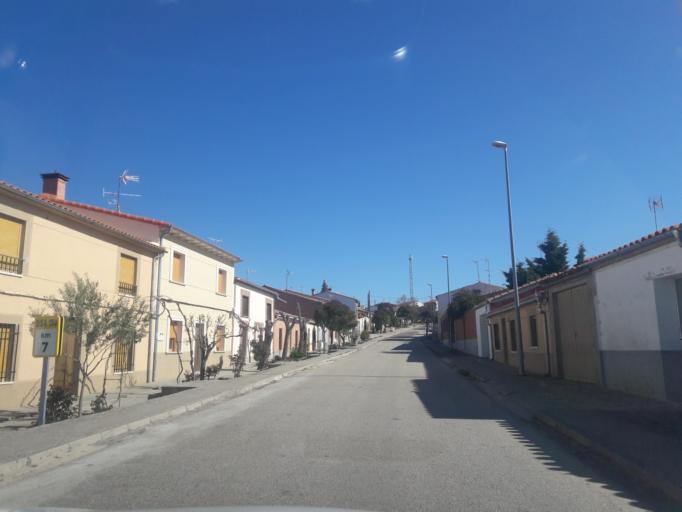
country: ES
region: Castille and Leon
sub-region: Provincia de Salamanca
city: Mancera de Abajo
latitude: 40.8403
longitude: -5.2008
